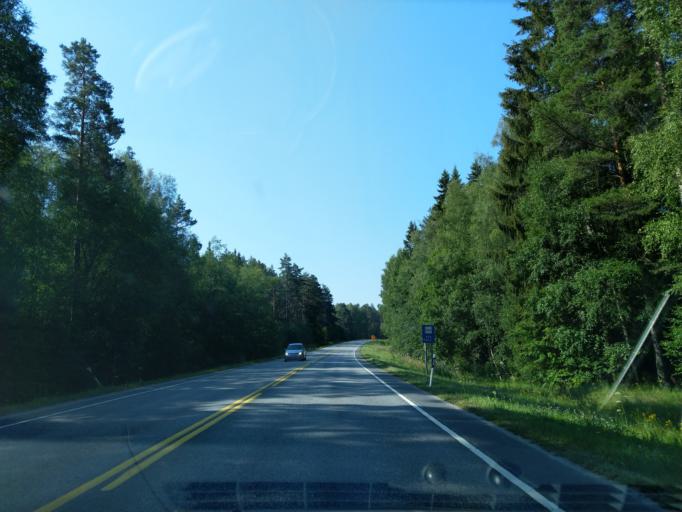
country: FI
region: Satakunta
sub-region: Pori
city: Noormarkku
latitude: 61.6024
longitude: 21.8775
